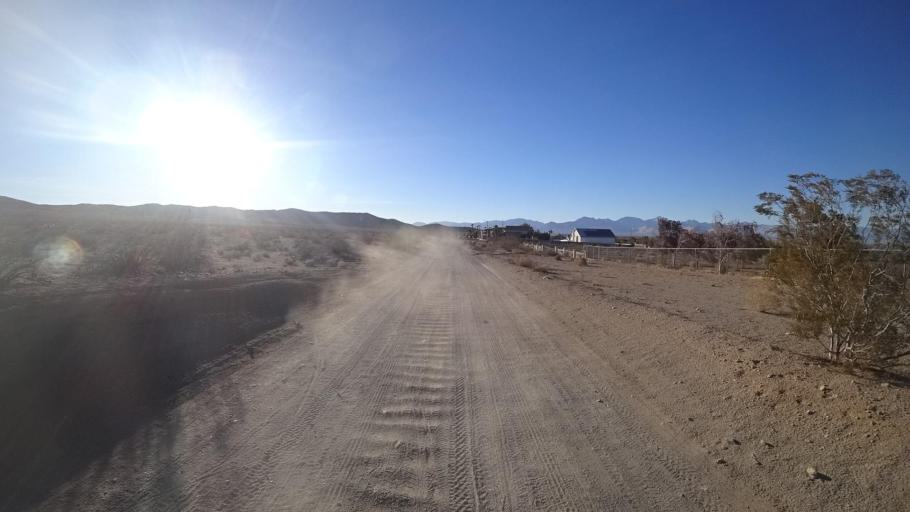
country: US
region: California
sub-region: Kern County
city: Ridgecrest
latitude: 35.5784
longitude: -117.6692
